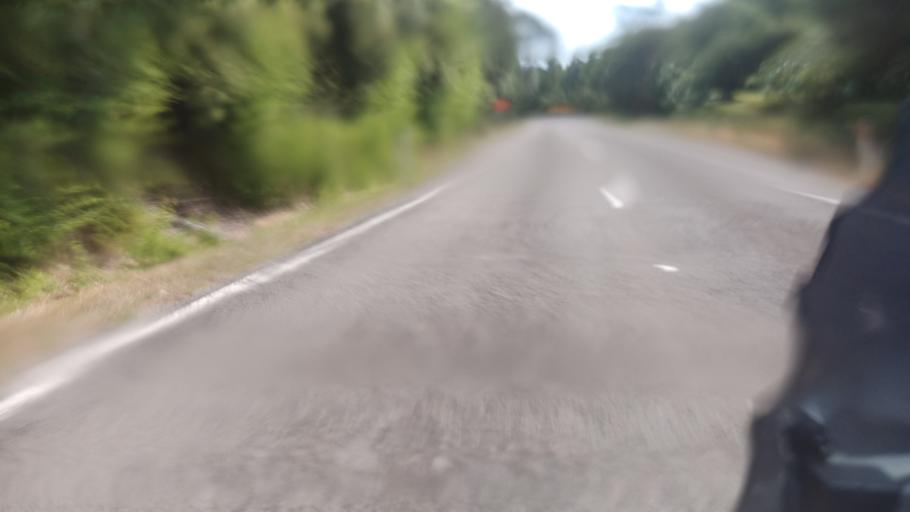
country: NZ
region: Bay of Plenty
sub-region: Opotiki District
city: Opotiki
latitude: -37.5760
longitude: 178.1134
